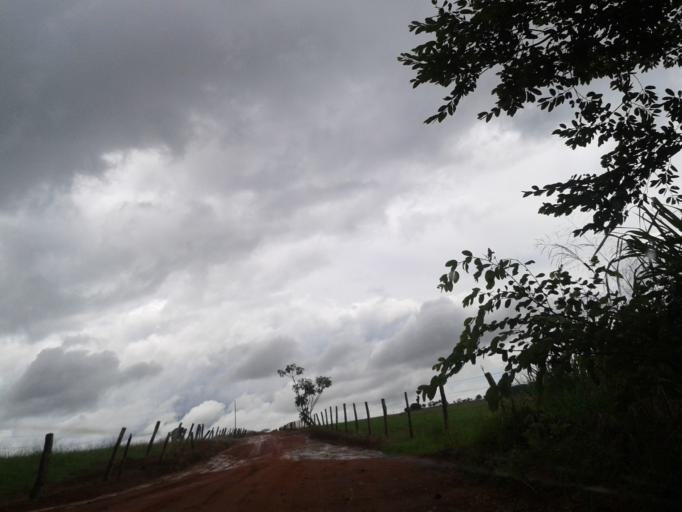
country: BR
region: Minas Gerais
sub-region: Santa Vitoria
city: Santa Vitoria
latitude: -18.6733
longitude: -49.9323
